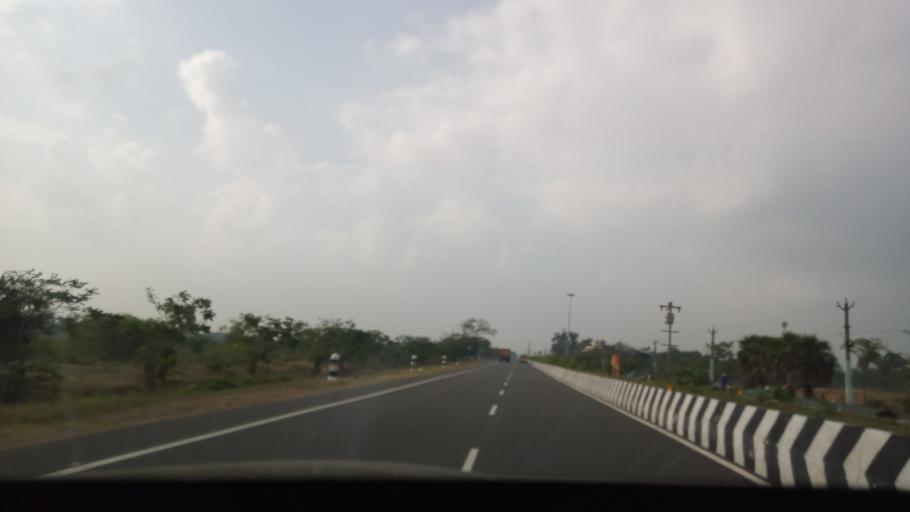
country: IN
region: Tamil Nadu
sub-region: Kancheepuram
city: Injambakkam
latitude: 12.7657
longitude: 80.2464
